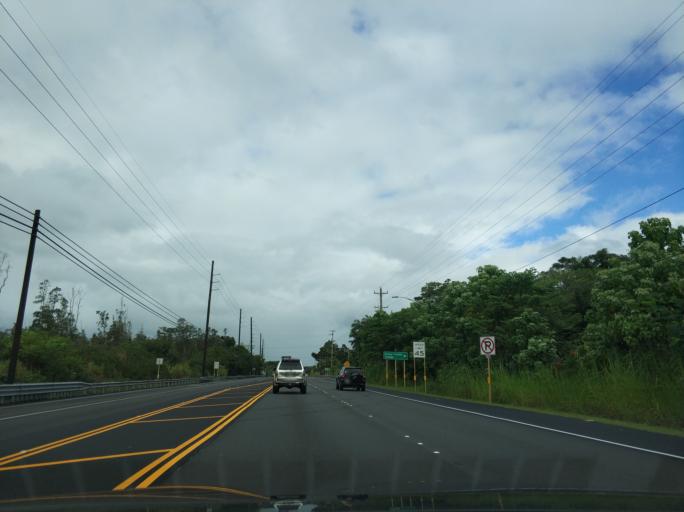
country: US
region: Hawaii
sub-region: Hawaii County
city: Kea'au
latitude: 19.6031
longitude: -155.0250
